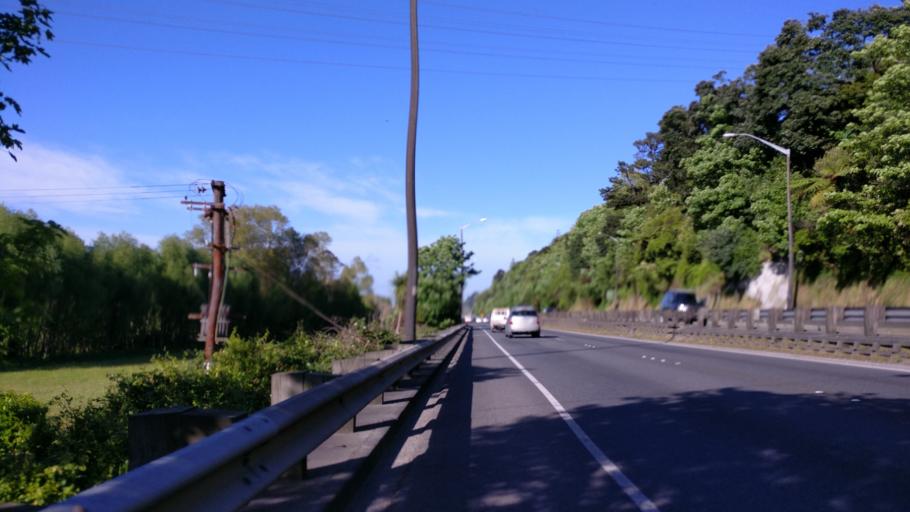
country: NZ
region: Wellington
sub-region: Lower Hutt City
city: Lower Hutt
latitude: -41.1989
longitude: 174.9138
